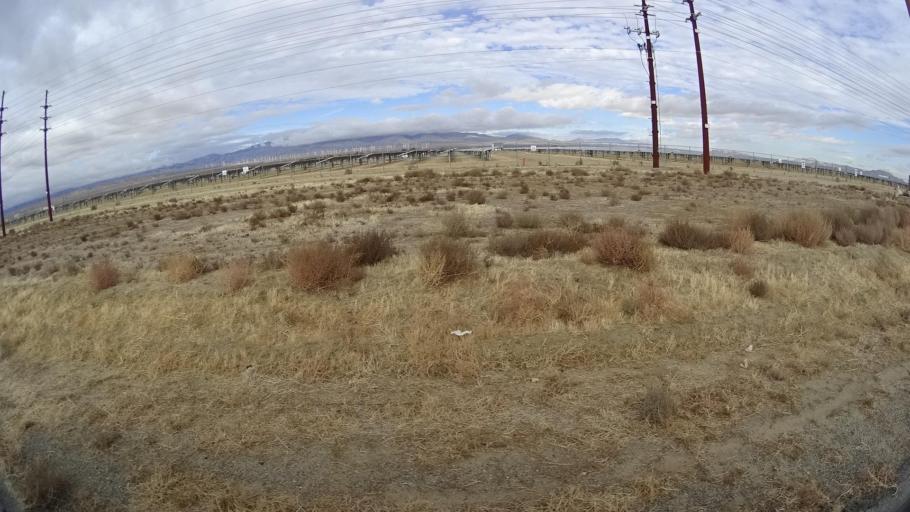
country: US
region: California
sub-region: Los Angeles County
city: Green Valley
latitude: 34.8192
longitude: -118.4006
